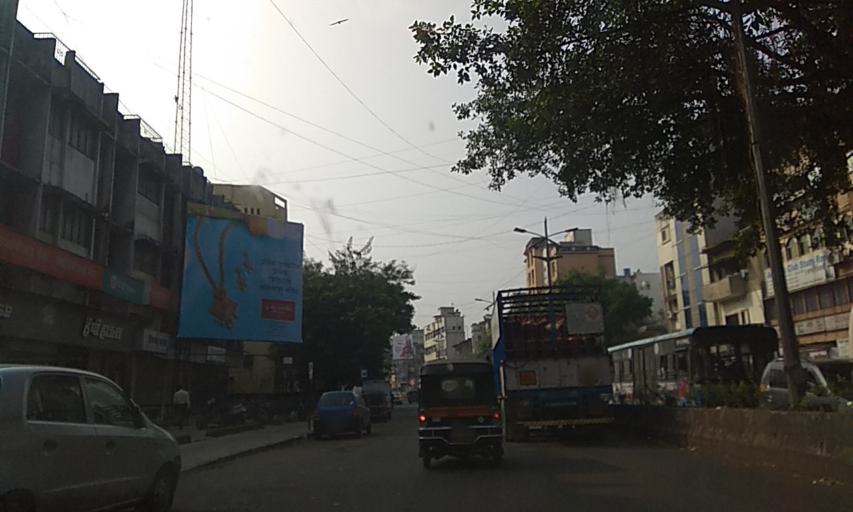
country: IN
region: Maharashtra
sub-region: Pune Division
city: Pune
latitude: 18.5110
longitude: 73.8432
